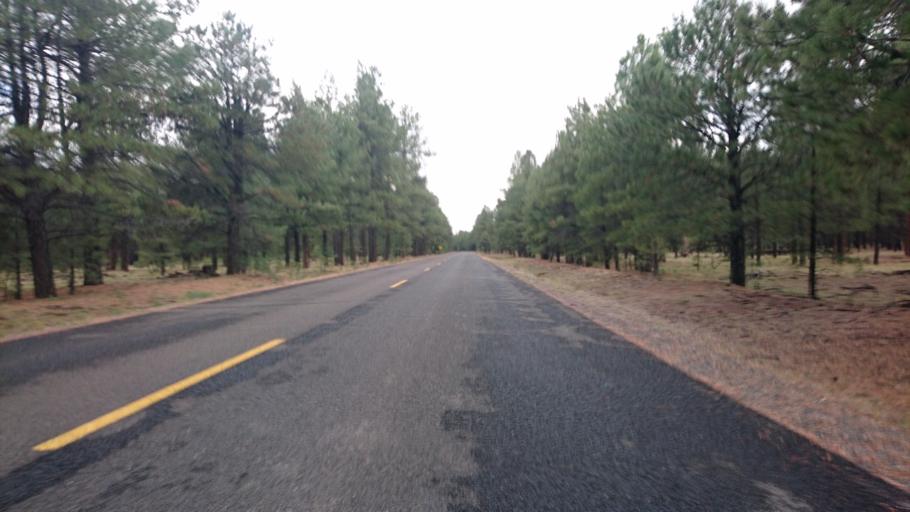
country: US
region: Arizona
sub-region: Coconino County
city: Parks
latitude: 35.2606
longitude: -111.8709
